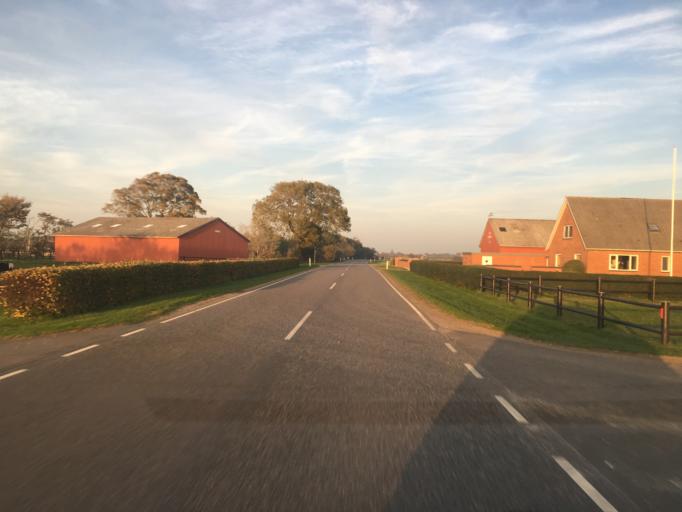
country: DK
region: South Denmark
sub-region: Tonder Kommune
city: Logumkloster
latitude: 55.0450
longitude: 9.0380
